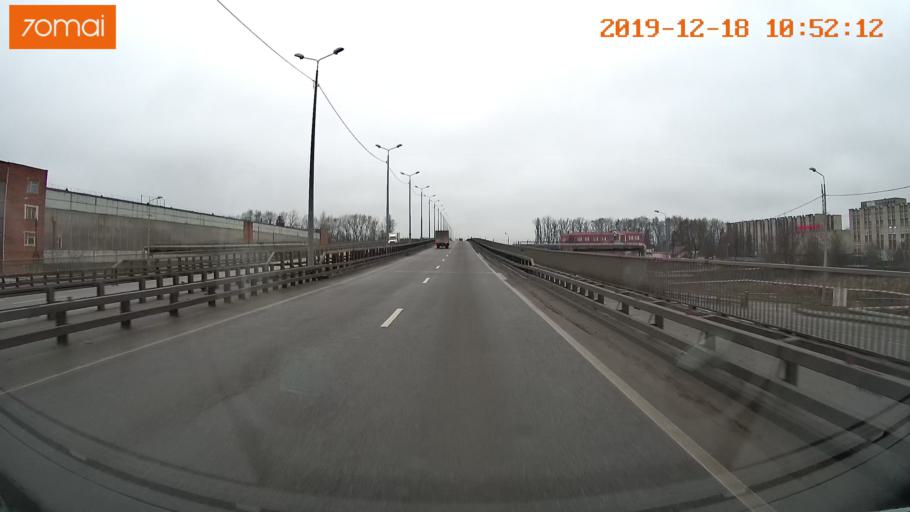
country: RU
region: Moskovskaya
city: Selyatino
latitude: 55.5222
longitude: 36.9852
